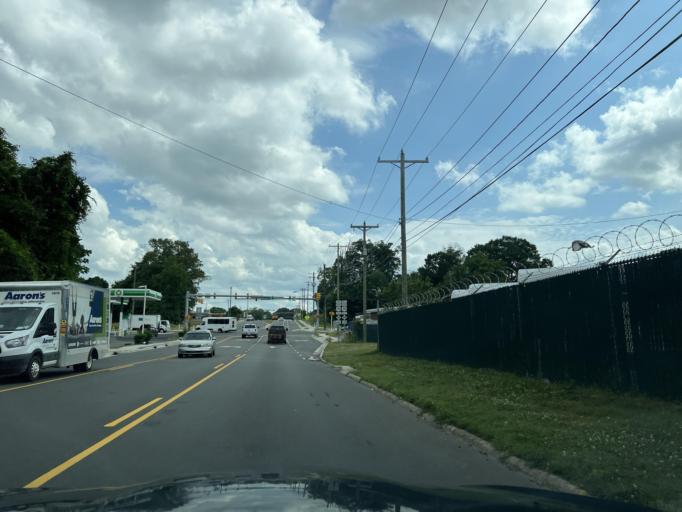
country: US
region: North Carolina
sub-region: Durham County
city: Durham
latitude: 35.9954
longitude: -78.8860
